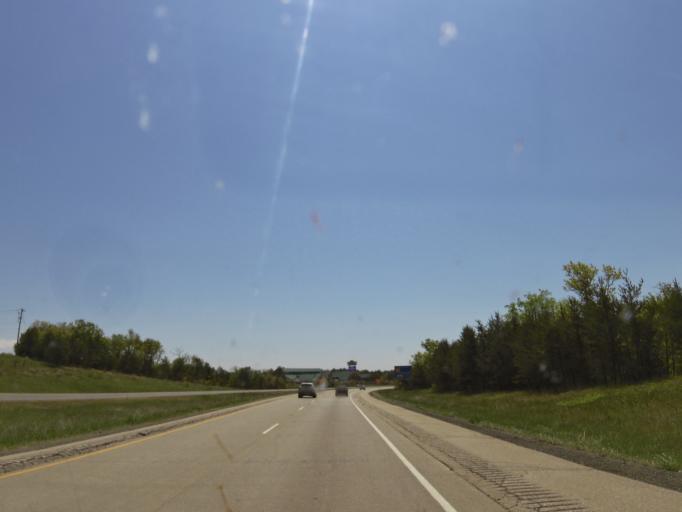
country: US
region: Wisconsin
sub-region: Monroe County
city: Tomah
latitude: 44.1354
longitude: -90.5369
